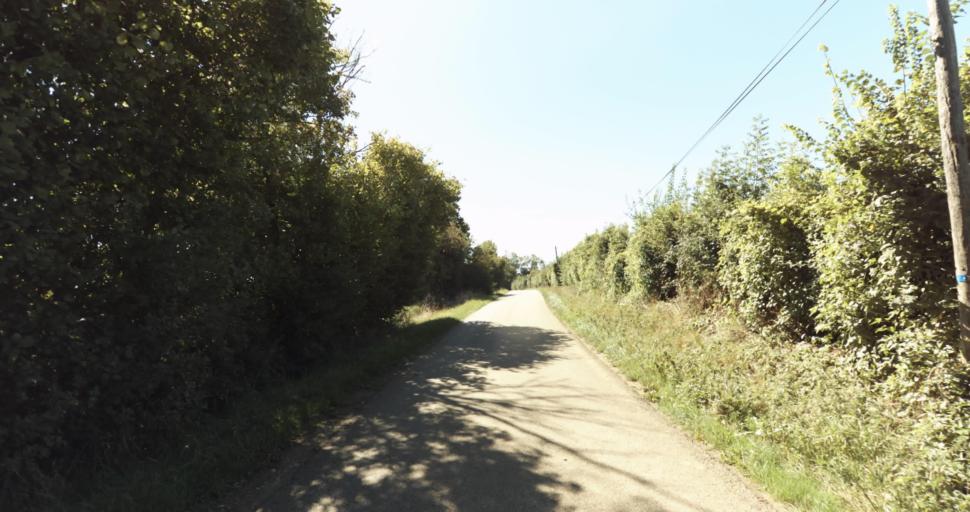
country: FR
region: Lower Normandy
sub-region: Departement de l'Orne
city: Gace
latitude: 48.7872
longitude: 0.2851
